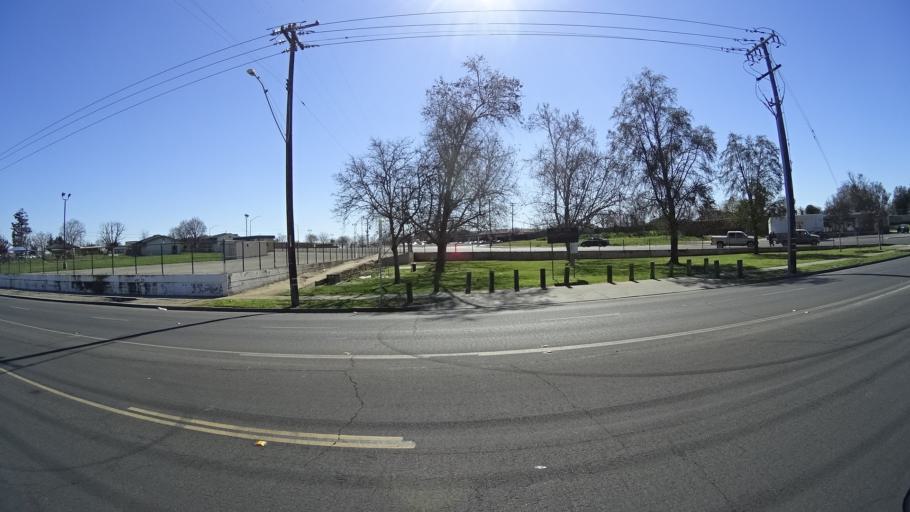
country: US
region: California
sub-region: Fresno County
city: West Park
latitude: 36.7217
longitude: -119.8120
